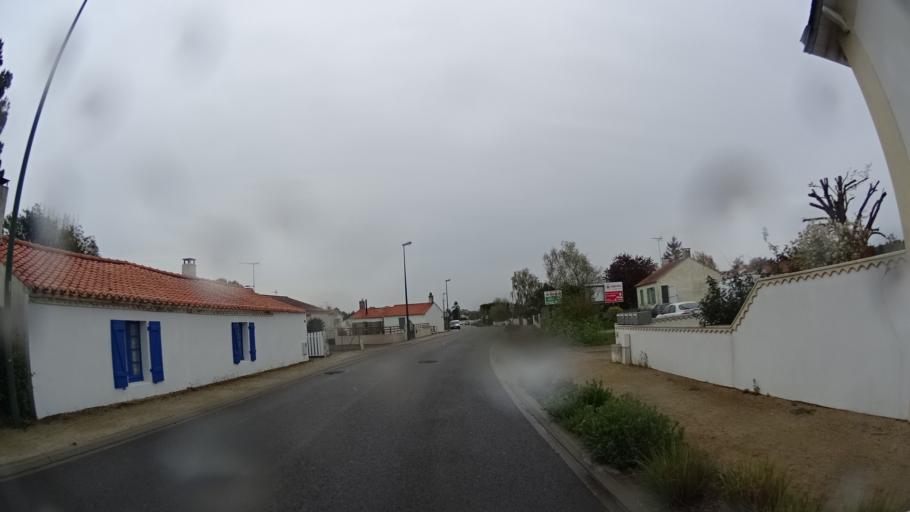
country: FR
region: Pays de la Loire
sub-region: Departement de la Vendee
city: La Barre-de-Monts
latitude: 46.8825
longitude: -2.1193
